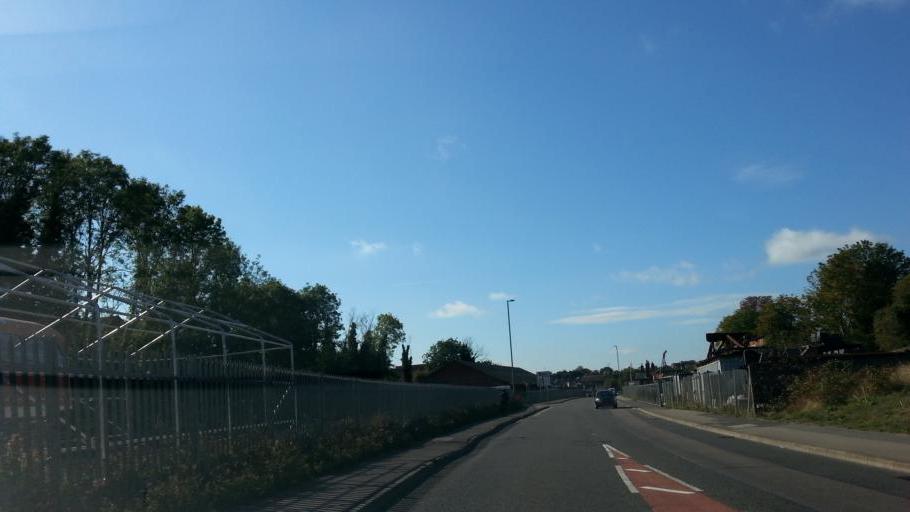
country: GB
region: England
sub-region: Northamptonshire
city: Rushden
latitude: 52.2954
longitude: -0.5950
